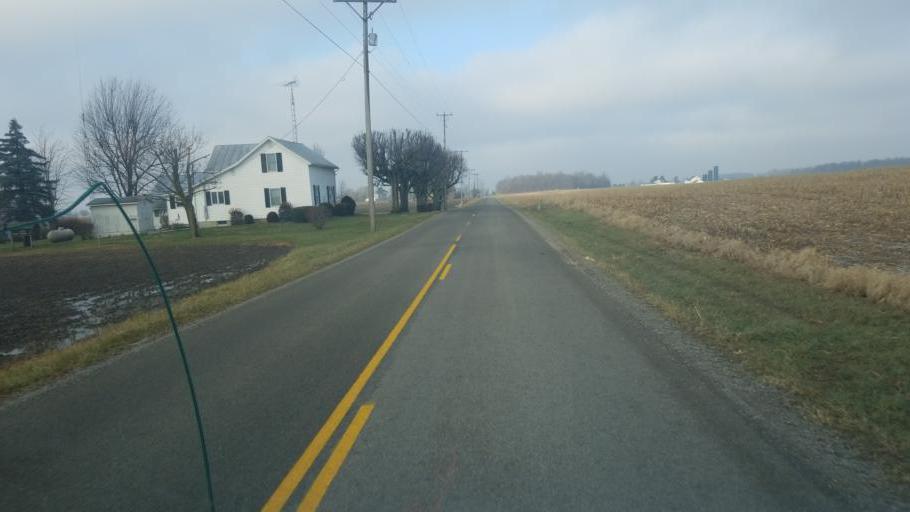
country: US
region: Ohio
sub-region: Hardin County
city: Kenton
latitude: 40.6778
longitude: -83.5761
